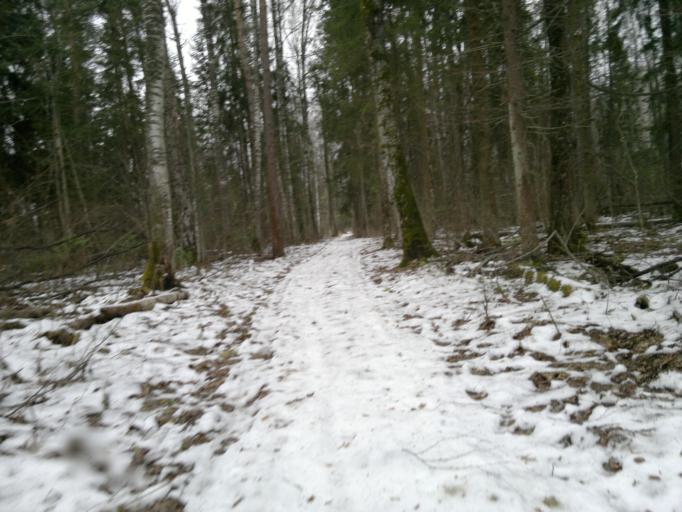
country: RU
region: Mariy-El
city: Yoshkar-Ola
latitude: 56.6088
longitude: 47.9574
